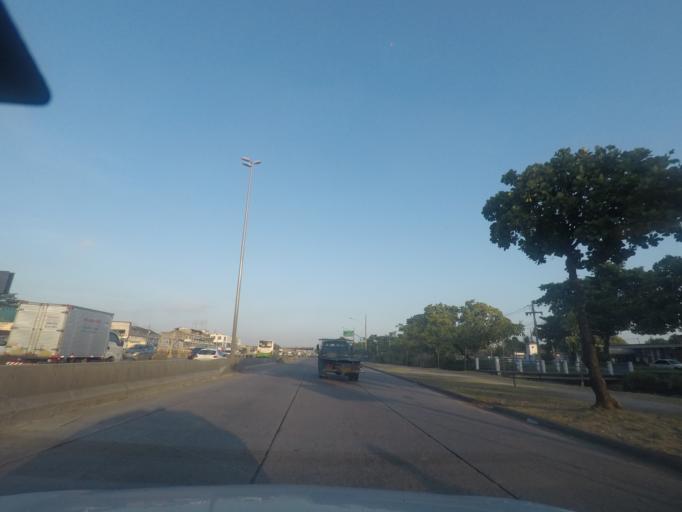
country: BR
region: Rio de Janeiro
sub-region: Duque De Caxias
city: Duque de Caxias
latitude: -22.8290
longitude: -43.2715
